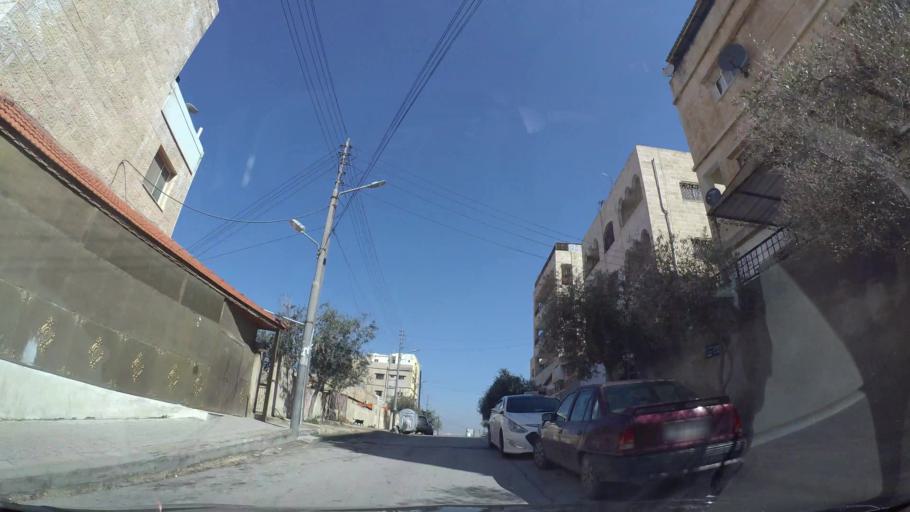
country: JO
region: Amman
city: Amman
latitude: 31.9891
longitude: 35.9843
